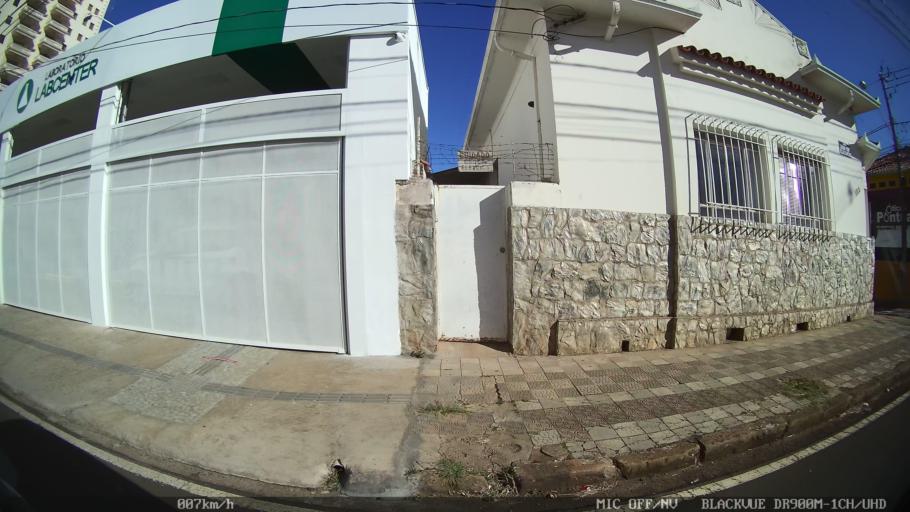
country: BR
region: Sao Paulo
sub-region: Franca
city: Franca
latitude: -20.5398
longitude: -47.4037
